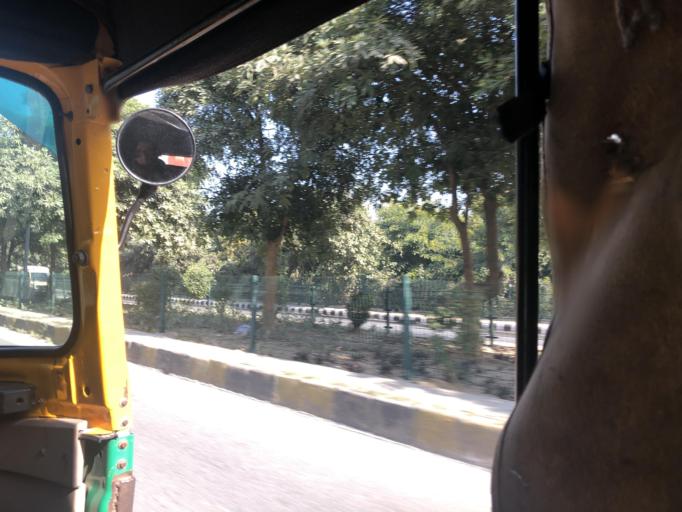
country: IN
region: Haryana
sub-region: Gurgaon
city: Gurgaon
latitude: 28.4348
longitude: 77.0906
